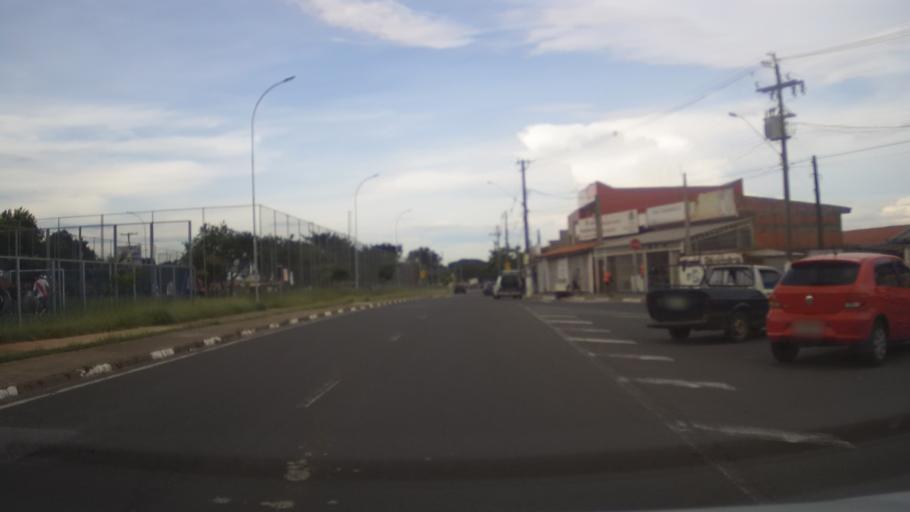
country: BR
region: Sao Paulo
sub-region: Hortolandia
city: Hortolandia
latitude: -22.9567
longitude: -47.1901
